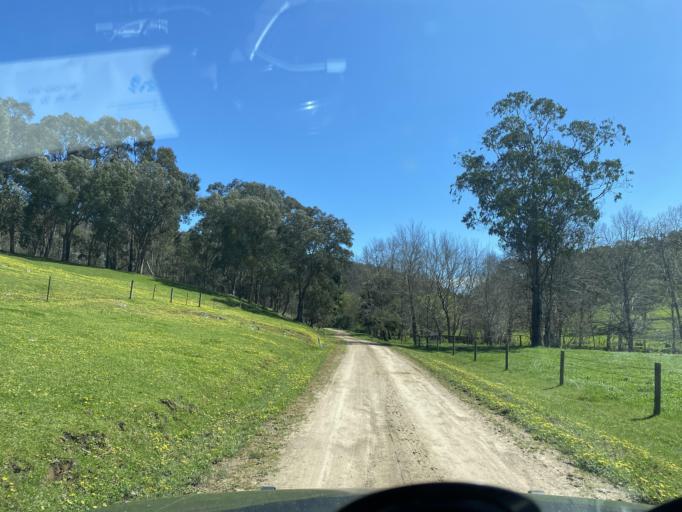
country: AU
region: Victoria
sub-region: Benalla
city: Benalla
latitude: -36.7106
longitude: 146.1802
